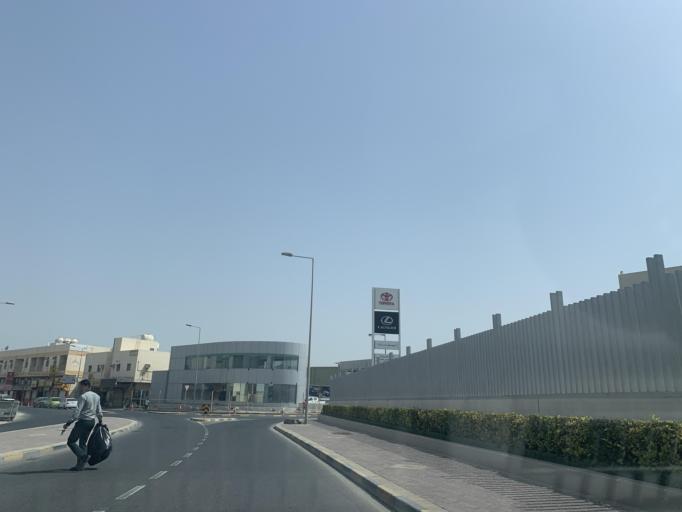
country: BH
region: Northern
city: Madinat `Isa
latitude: 26.1887
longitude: 50.5402
